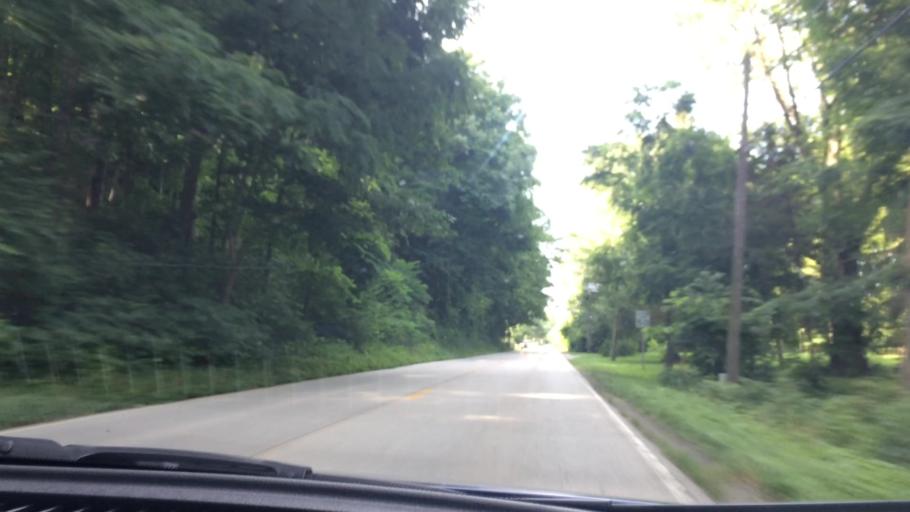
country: US
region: Indiana
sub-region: Tippecanoe County
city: West Lafayette
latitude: 40.4385
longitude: -86.8972
